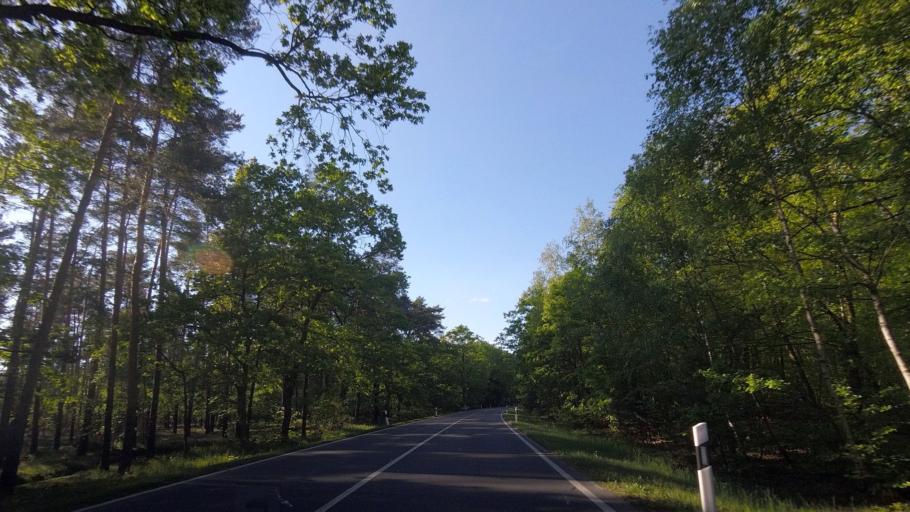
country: DE
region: Brandenburg
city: Luebben
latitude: 51.8983
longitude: 13.8950
